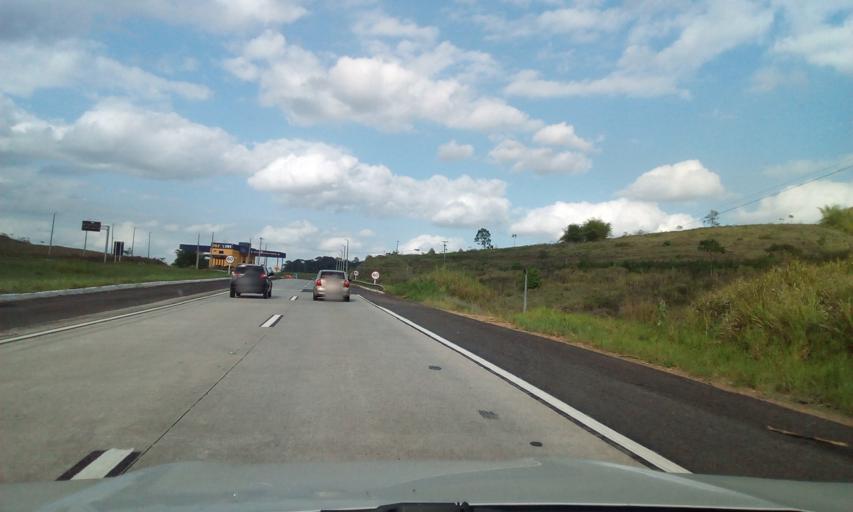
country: BR
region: Pernambuco
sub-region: Joaquim Nabuco
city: Joaquim Nabuco
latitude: -8.5745
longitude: -35.4824
